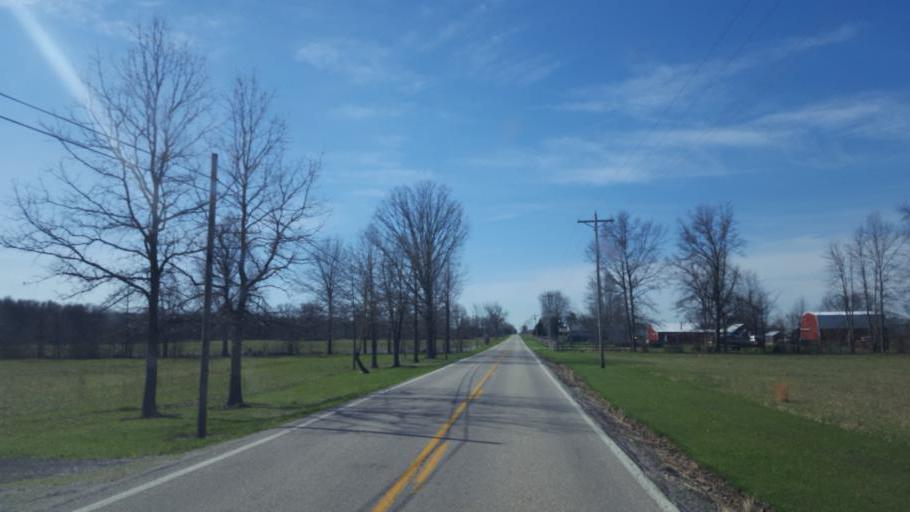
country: US
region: Ohio
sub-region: Morrow County
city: Cardington
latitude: 40.5370
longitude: -82.9626
